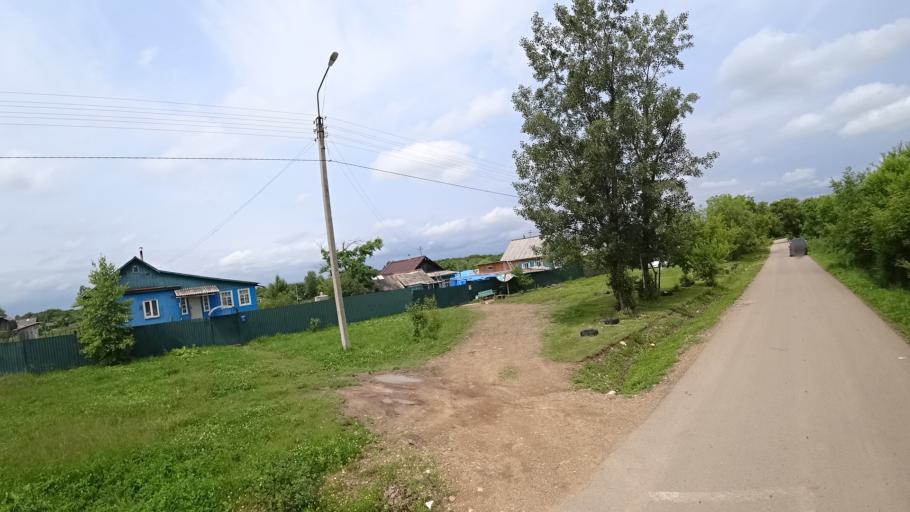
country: RU
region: Primorskiy
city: Novosysoyevka
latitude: 44.2374
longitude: 133.3584
